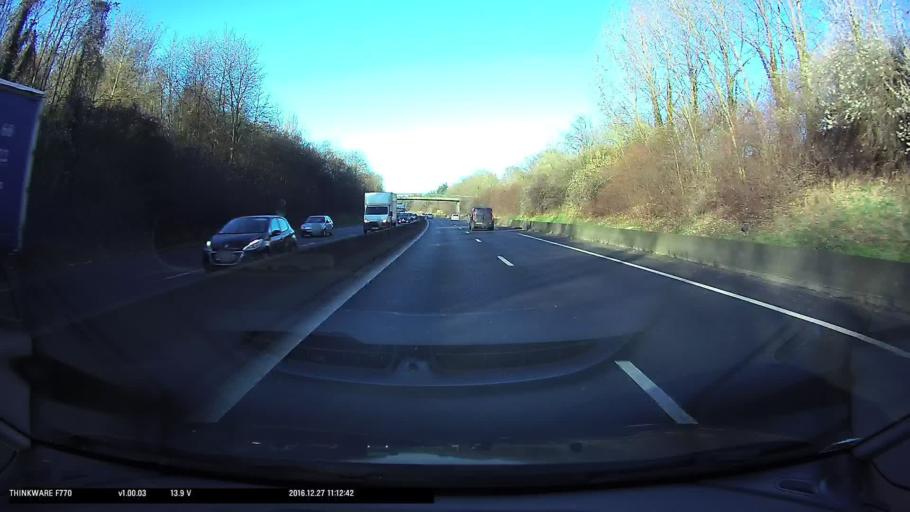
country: FR
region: Ile-de-France
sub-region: Departement du Val-d'Oise
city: Osny
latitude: 49.0520
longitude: 2.0648
